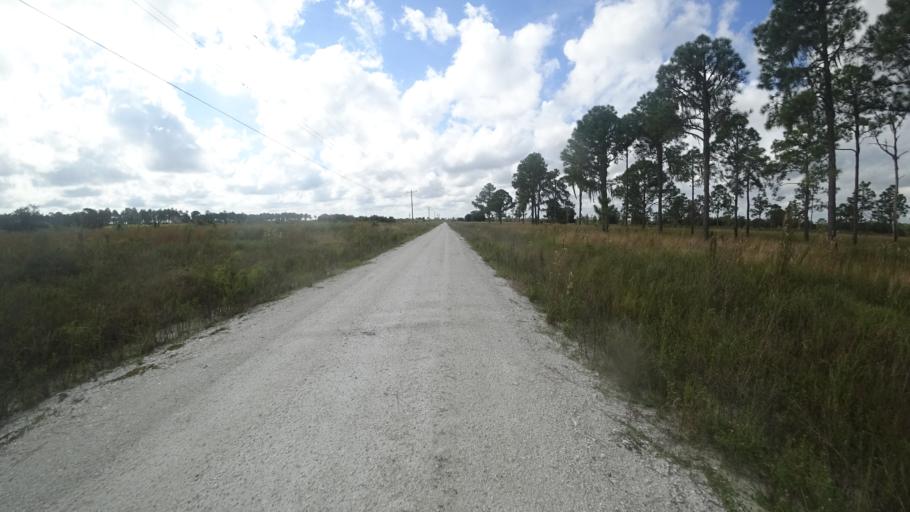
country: US
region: Florida
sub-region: Hillsborough County
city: Wimauma
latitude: 27.5412
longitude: -82.1282
